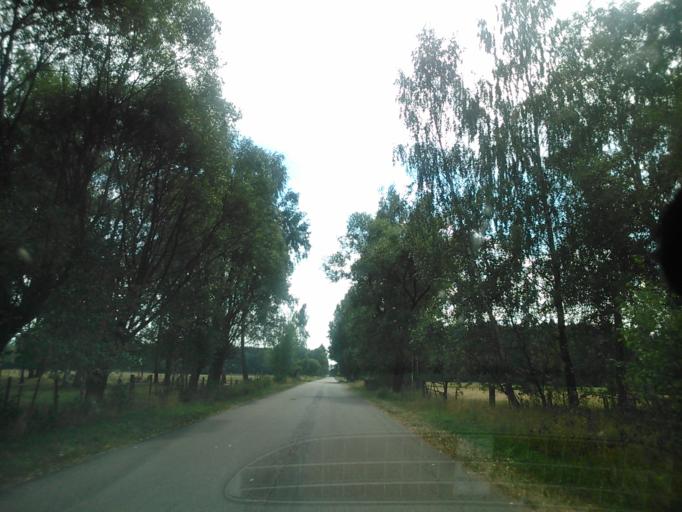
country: PL
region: Masovian Voivodeship
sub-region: Powiat ostrolecki
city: Czarnia
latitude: 53.3808
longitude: 21.2004
